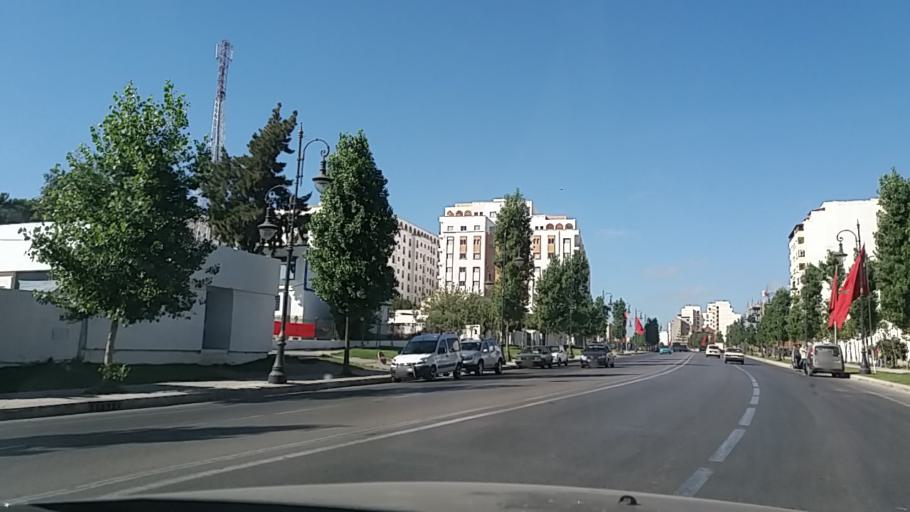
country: MA
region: Tanger-Tetouan
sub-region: Tanger-Assilah
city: Tangier
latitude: 35.7565
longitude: -5.8480
